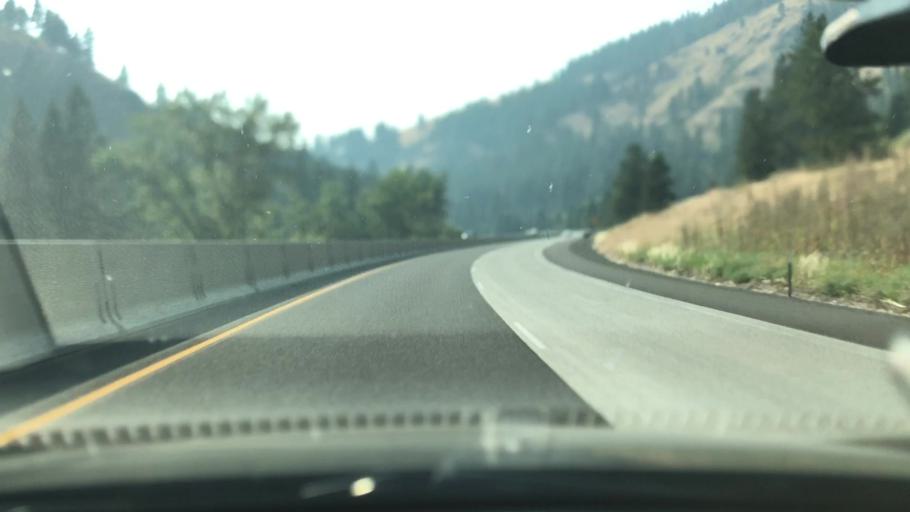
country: US
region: Oregon
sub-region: Union County
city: La Grande
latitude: 45.3529
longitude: -118.1828
